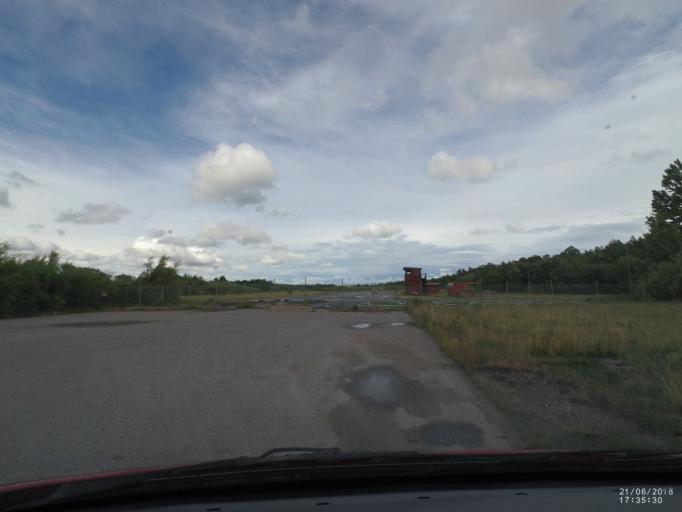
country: SE
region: Soedermanland
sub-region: Nykopings Kommun
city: Nykoping
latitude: 58.7458
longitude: 17.0516
